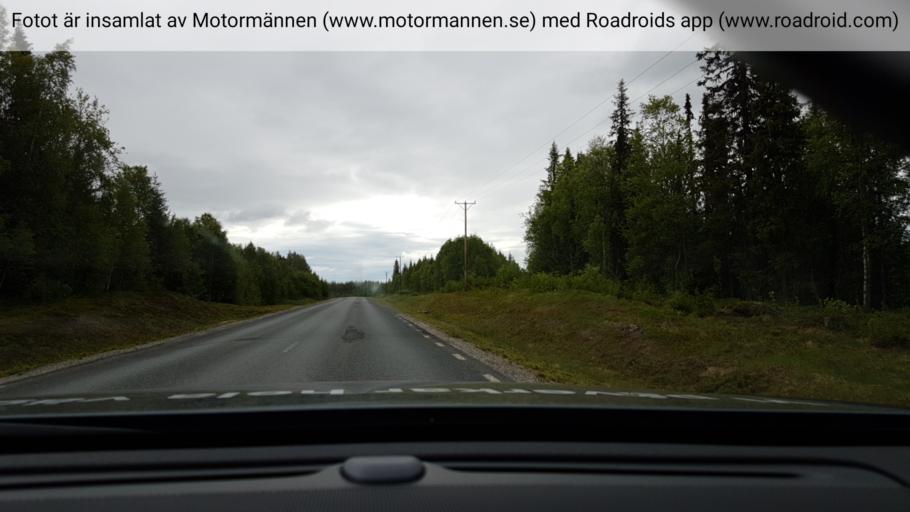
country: SE
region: Vaesterbotten
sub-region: Lycksele Kommun
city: Soderfors
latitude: 64.4720
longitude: 18.1931
